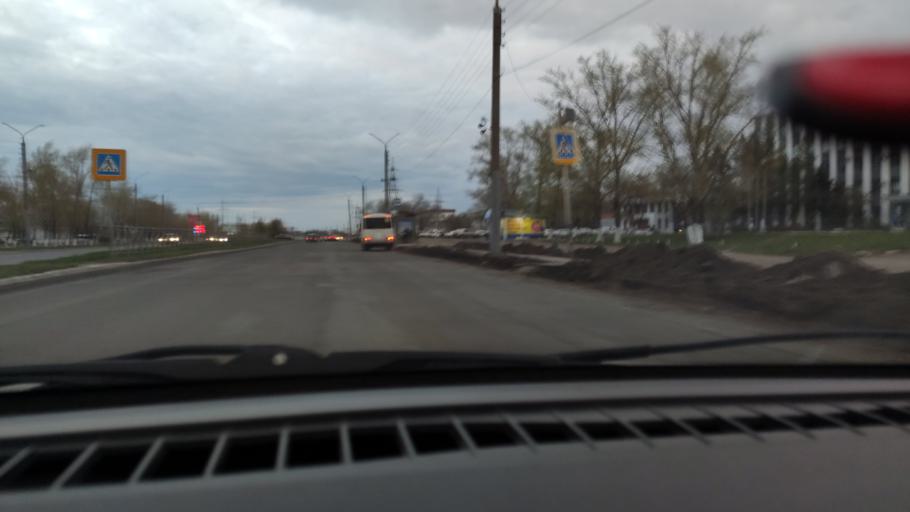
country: RU
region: Orenburg
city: Orenburg
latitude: 51.8220
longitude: 55.1078
